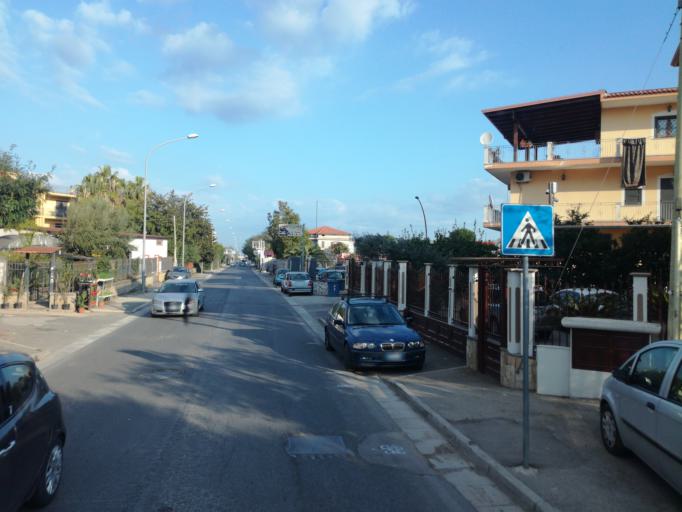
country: IT
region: Campania
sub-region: Provincia di Napoli
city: Giugliano in Campania
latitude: 40.9410
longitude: 14.1831
